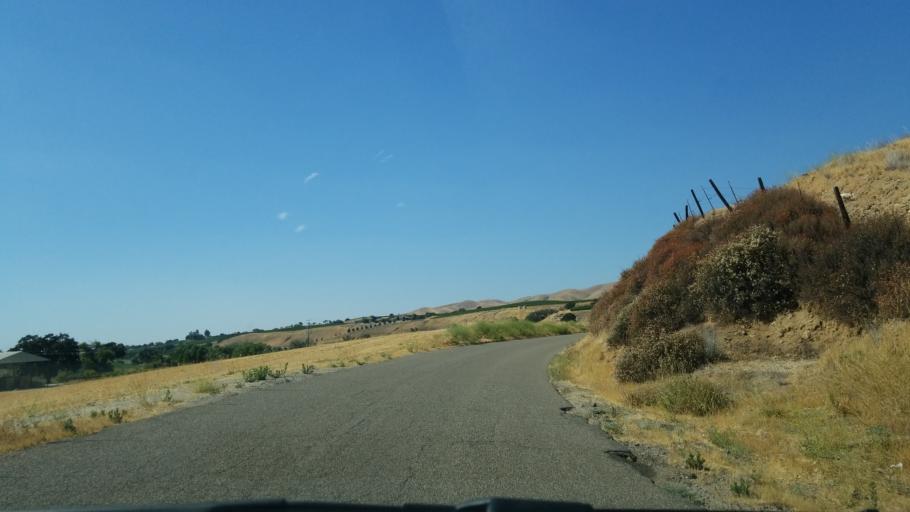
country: US
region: California
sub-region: San Luis Obispo County
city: San Miguel
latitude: 35.7237
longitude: -120.6548
